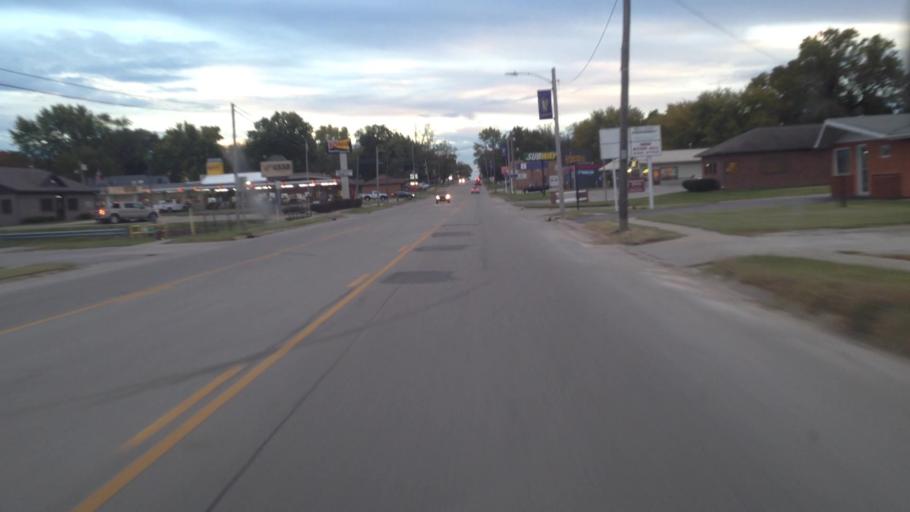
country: US
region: Kansas
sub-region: Anderson County
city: Garnett
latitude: 38.2860
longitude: -95.2493
